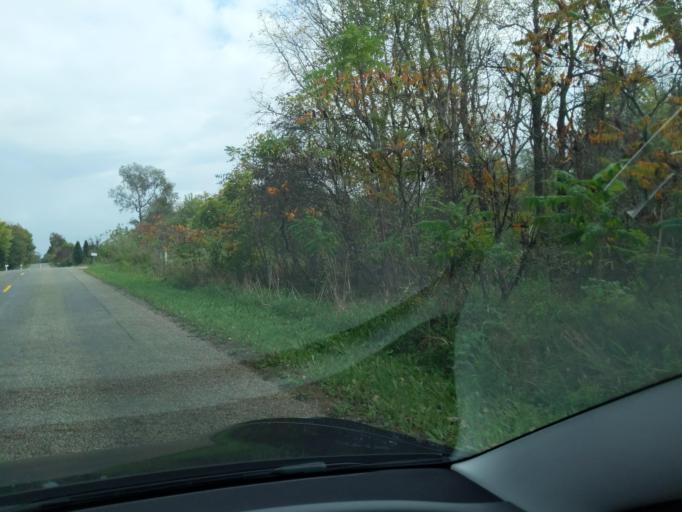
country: US
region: Michigan
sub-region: Eaton County
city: Eaton Rapids
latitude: 42.4656
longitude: -84.6082
